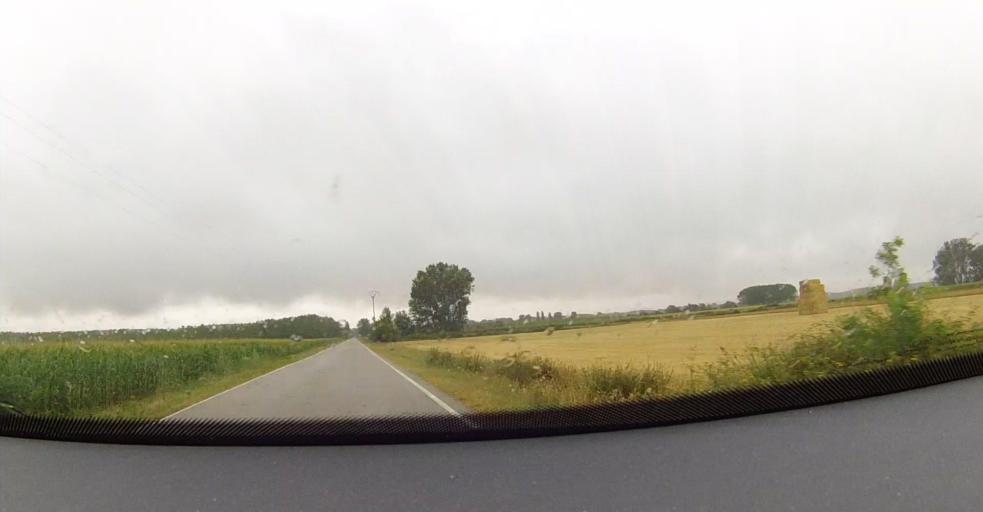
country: ES
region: Castille and Leon
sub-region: Provincia de Palencia
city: Pedrosa de la Vega
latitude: 42.4804
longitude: -4.7318
